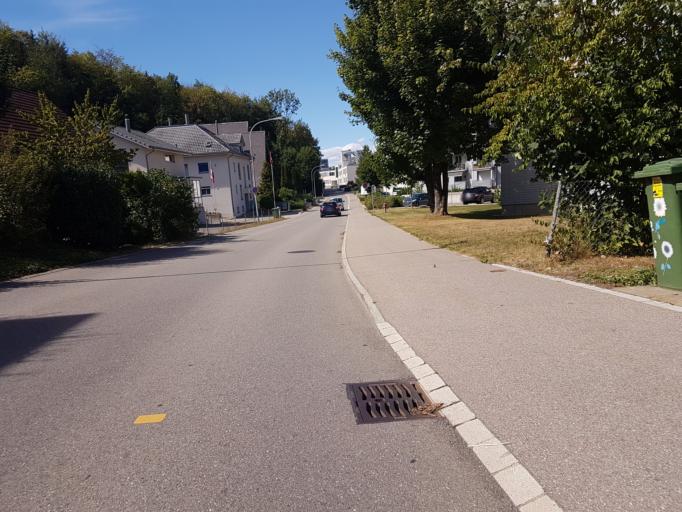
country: CH
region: Zurich
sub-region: Bezirk Pfaeffikon
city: Effretikon
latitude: 47.4217
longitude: 8.6909
